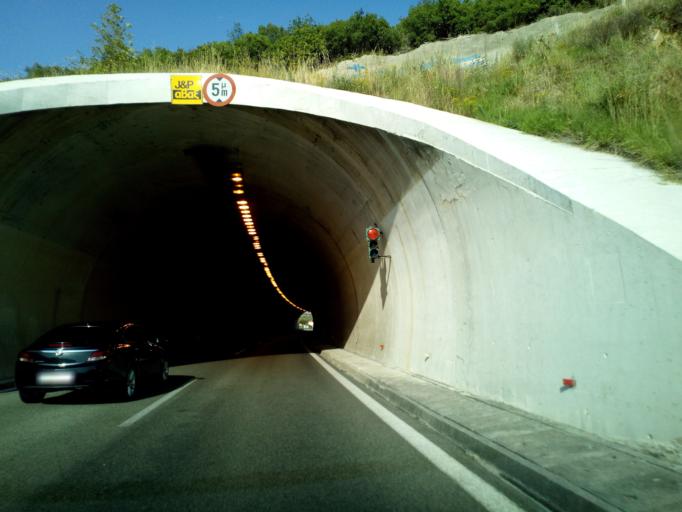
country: GR
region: Central Macedonia
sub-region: Nomos Thessalonikis
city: Nea Vrasna
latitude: 40.7009
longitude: 23.6482
